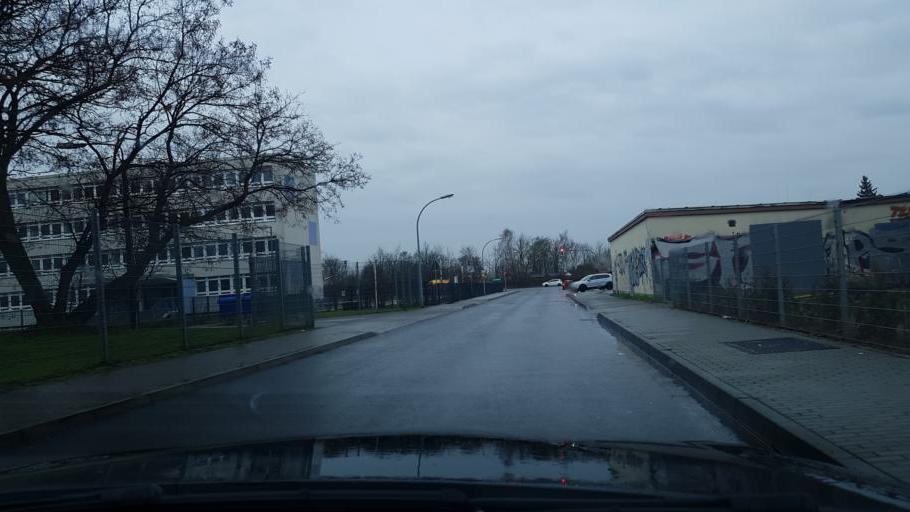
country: DE
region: Berlin
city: Altglienicke
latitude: 52.3961
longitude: 13.5336
